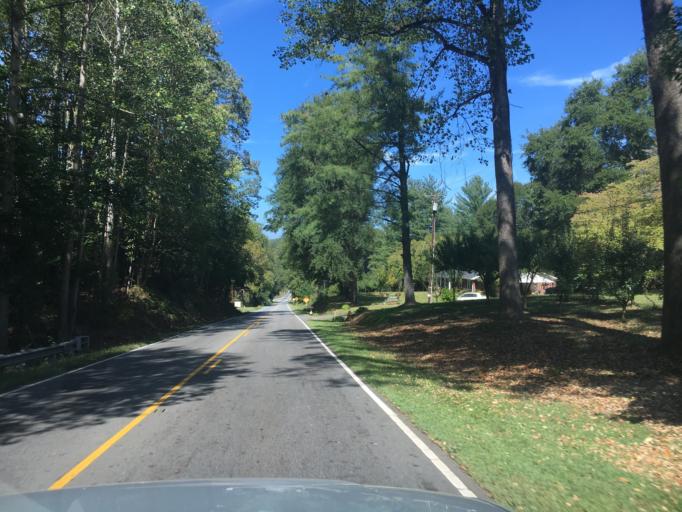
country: US
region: North Carolina
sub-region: Rutherford County
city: Rutherfordton
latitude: 35.3366
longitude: -81.9608
